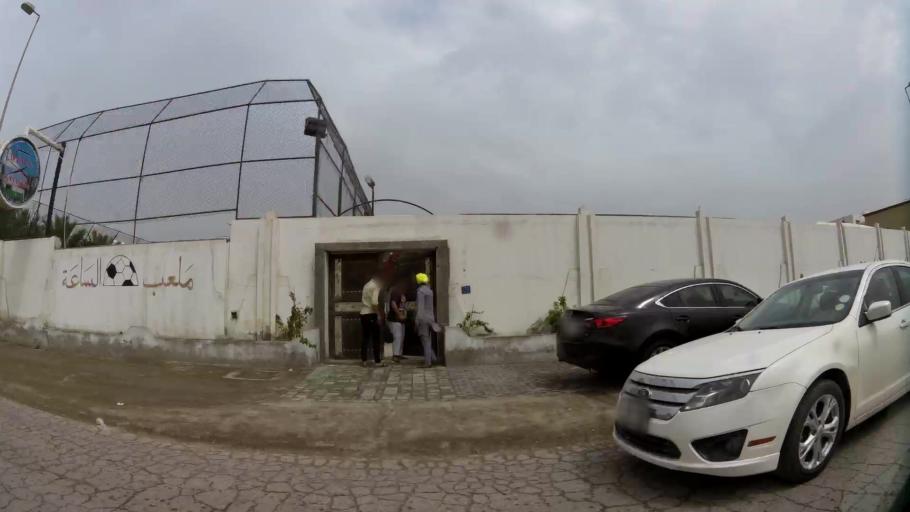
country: BH
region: Northern
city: Ar Rifa'
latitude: 26.1325
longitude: 50.5906
